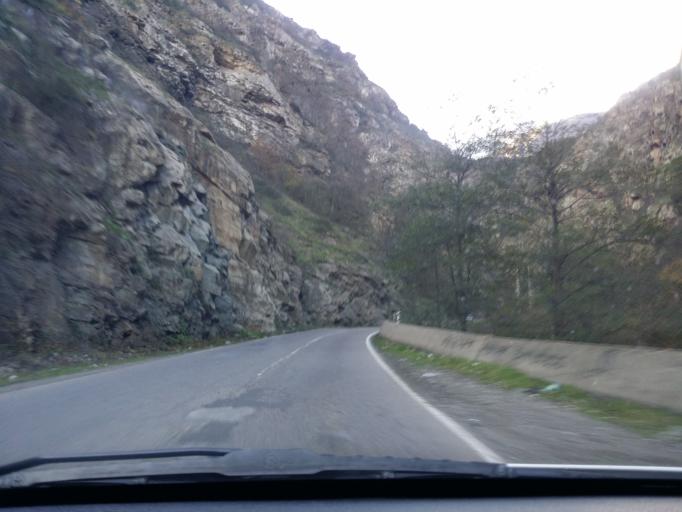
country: IR
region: Mazandaran
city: Chalus
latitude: 36.2988
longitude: 51.2472
